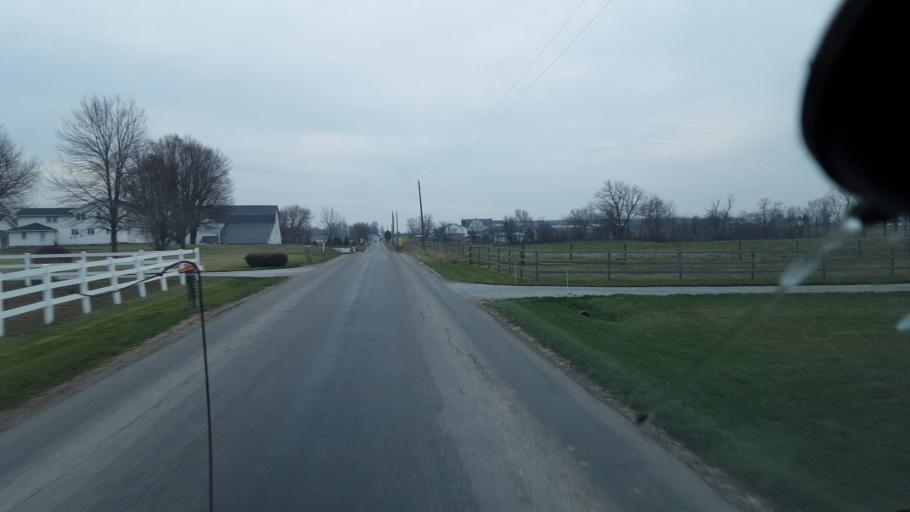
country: US
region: Indiana
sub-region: Elkhart County
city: Middlebury
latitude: 41.6821
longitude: -85.6197
